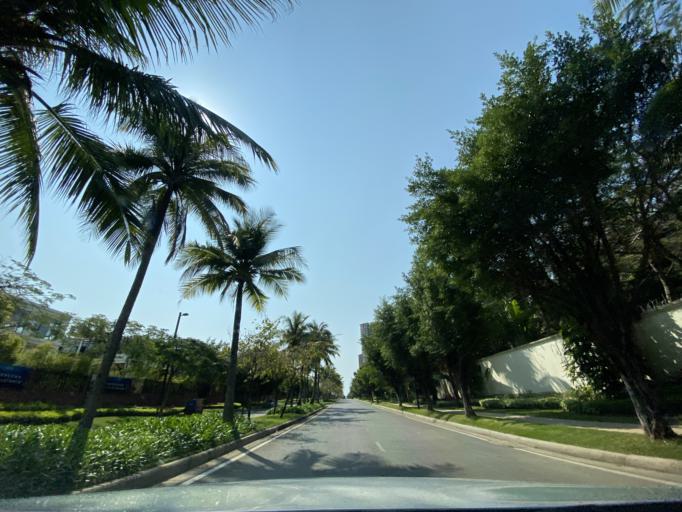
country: CN
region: Hainan
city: Yingzhou
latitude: 18.4176
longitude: 109.8885
